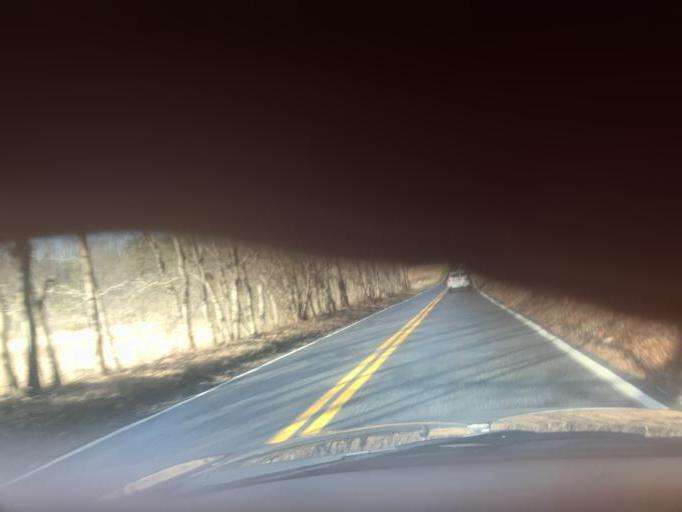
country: US
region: Maryland
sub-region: Montgomery County
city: Clarksburg
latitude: 39.2697
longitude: -77.2788
